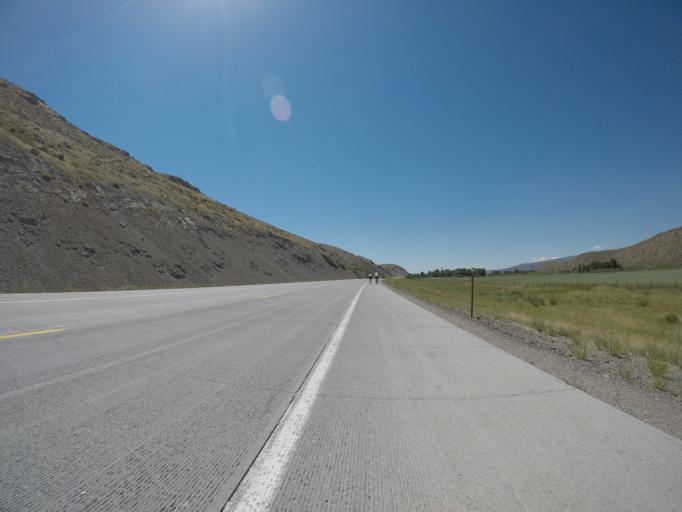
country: US
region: Idaho
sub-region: Bear Lake County
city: Montpelier
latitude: 42.1358
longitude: -110.9695
